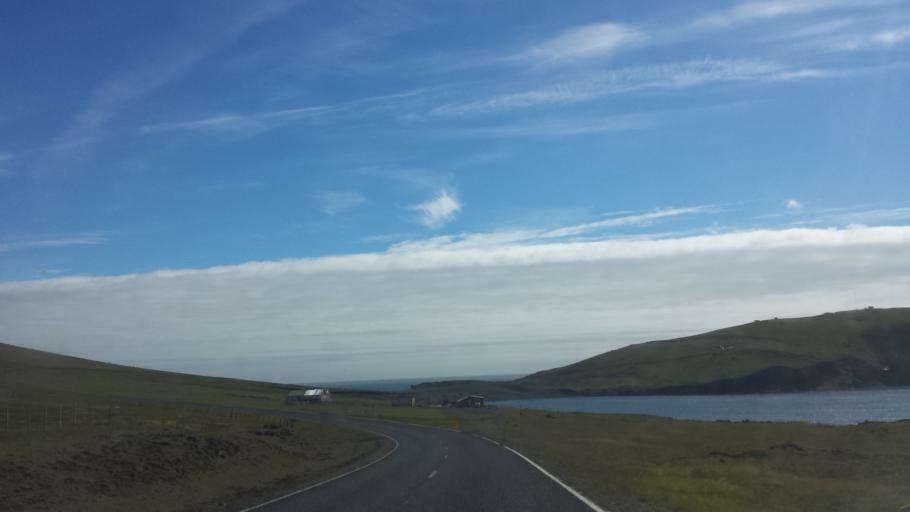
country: IS
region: South
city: Vestmannaeyjar
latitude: 63.4150
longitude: -20.2861
